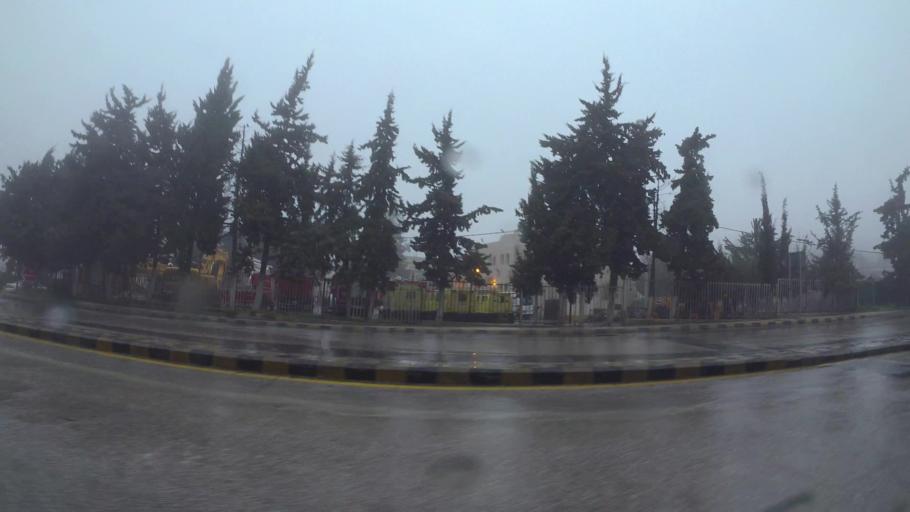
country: JO
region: Amman
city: Al Jubayhah
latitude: 32.0060
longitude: 35.8786
